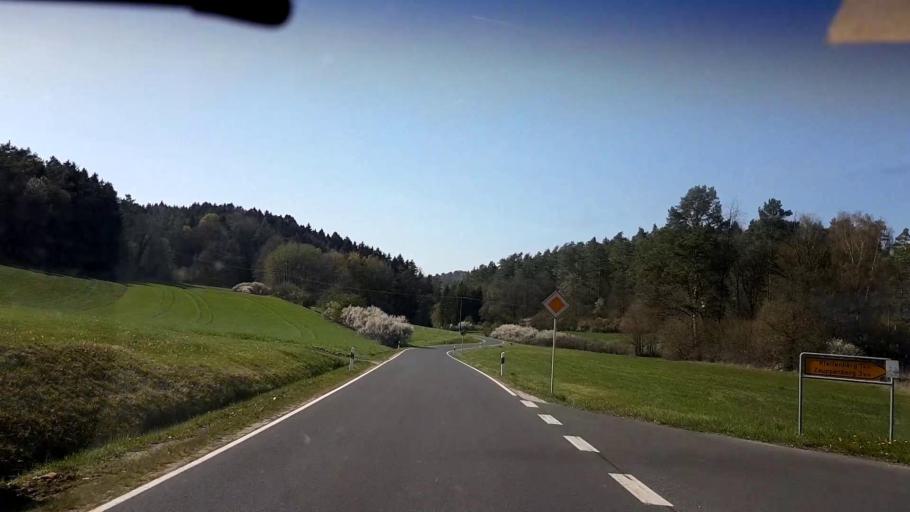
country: DE
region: Bavaria
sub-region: Upper Franconia
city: Waischenfeld
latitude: 49.8074
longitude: 11.3689
